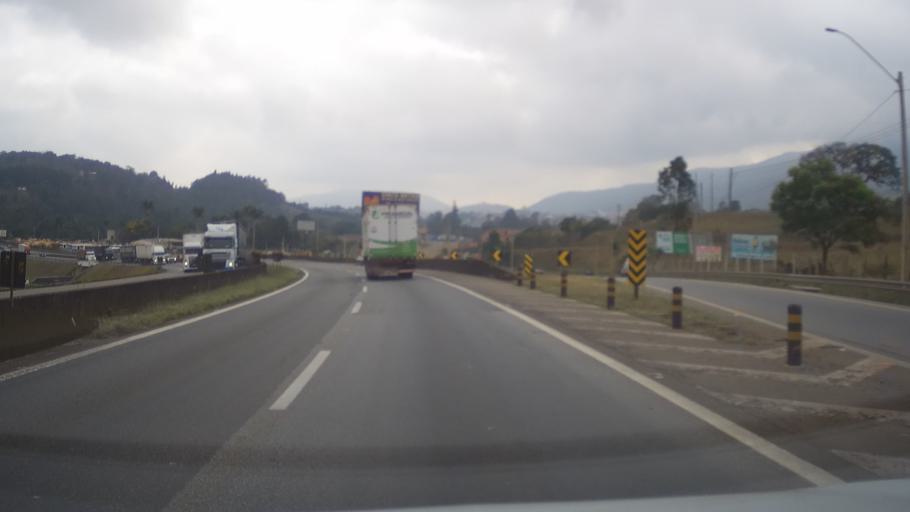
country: BR
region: Minas Gerais
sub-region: Extrema
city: Extrema
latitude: -22.8653
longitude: -46.3469
